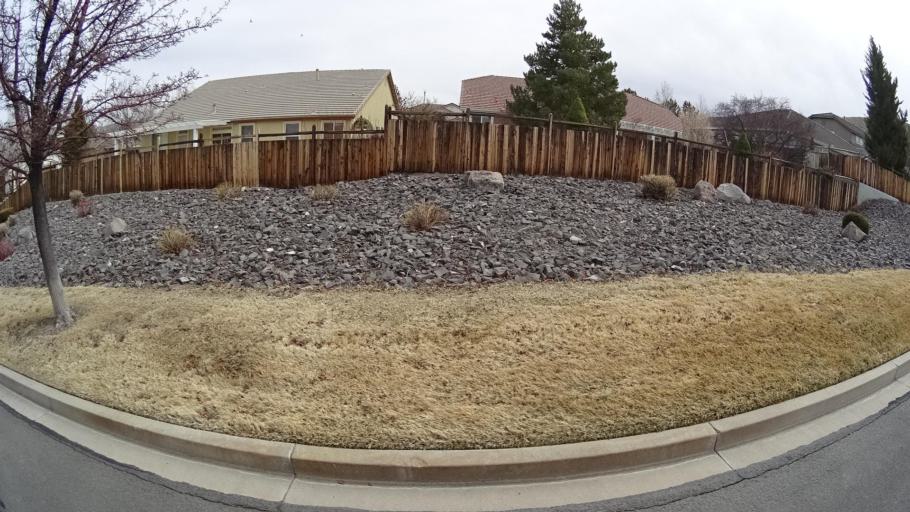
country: US
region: Nevada
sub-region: Washoe County
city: Spanish Springs
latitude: 39.6045
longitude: -119.6867
